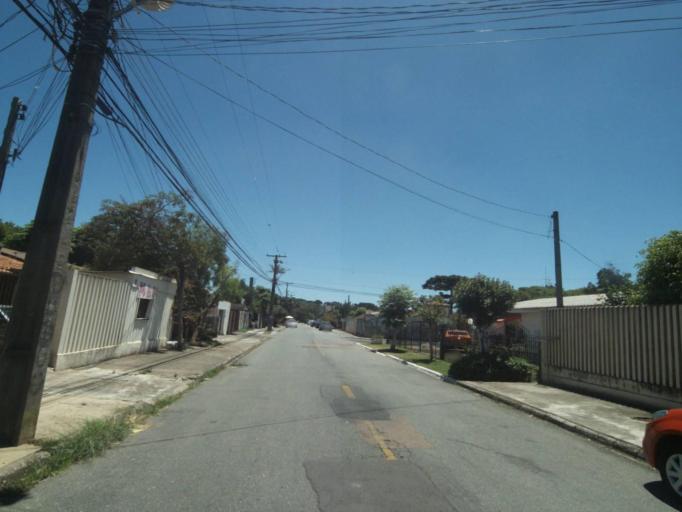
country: BR
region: Parana
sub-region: Curitiba
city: Curitiba
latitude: -25.4744
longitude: -49.3462
